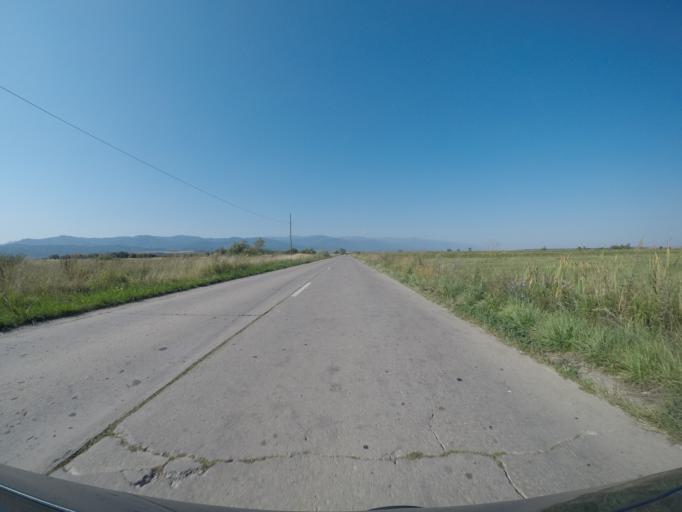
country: RO
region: Brasov
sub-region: Comuna Sinca Veche
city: Sinca Veche
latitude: 45.7730
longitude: 25.1824
